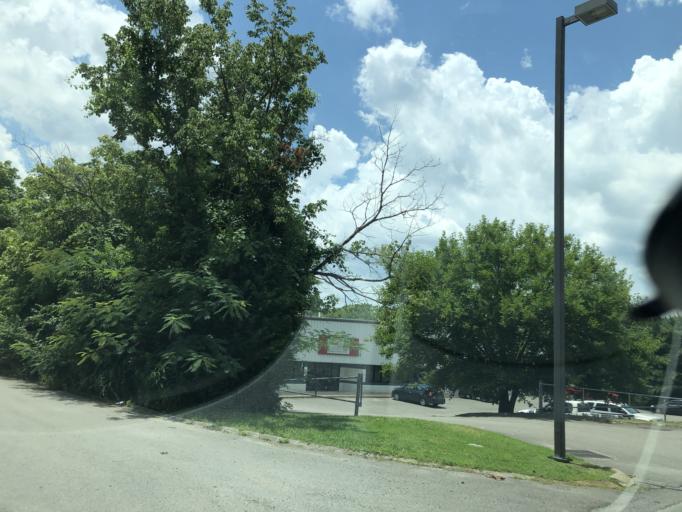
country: US
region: Tennessee
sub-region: Rutherford County
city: La Vergne
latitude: 36.0185
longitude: -86.6217
